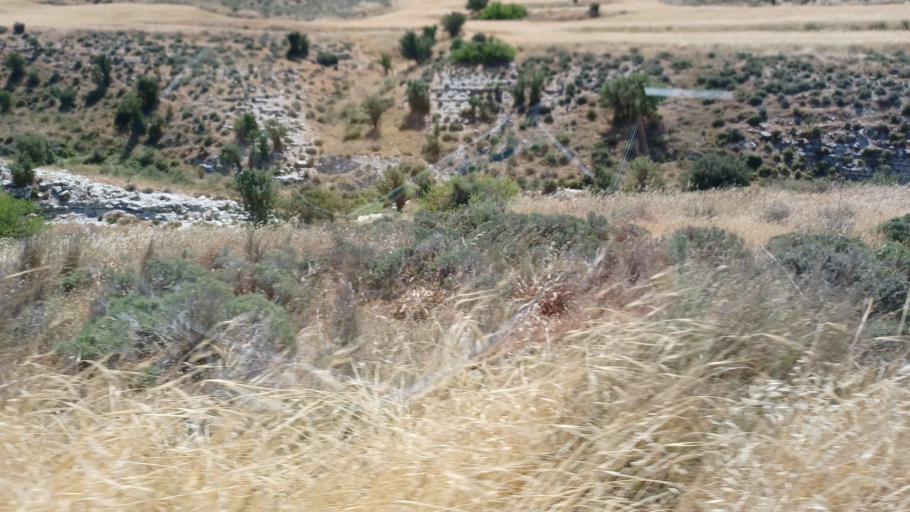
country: CY
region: Larnaka
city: Athienou
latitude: 34.9926
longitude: 33.5330
